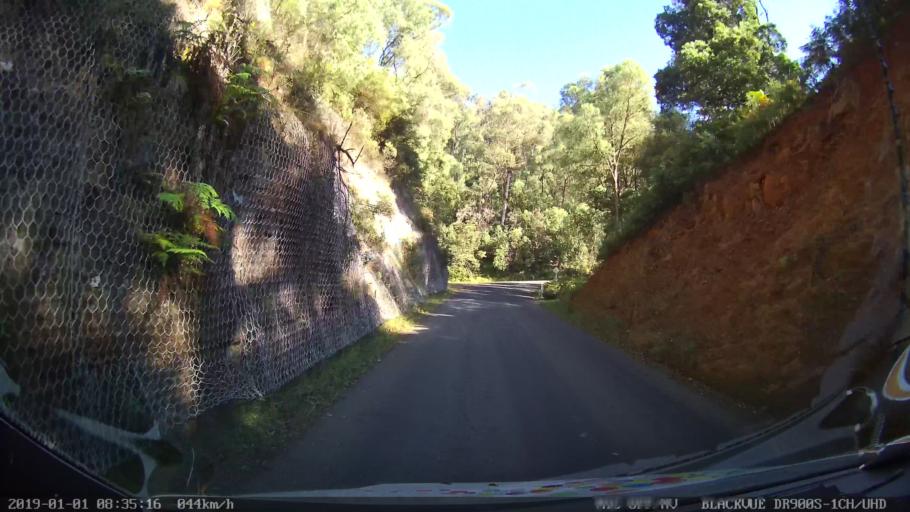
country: AU
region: New South Wales
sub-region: Snowy River
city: Jindabyne
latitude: -36.3499
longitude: 148.1933
